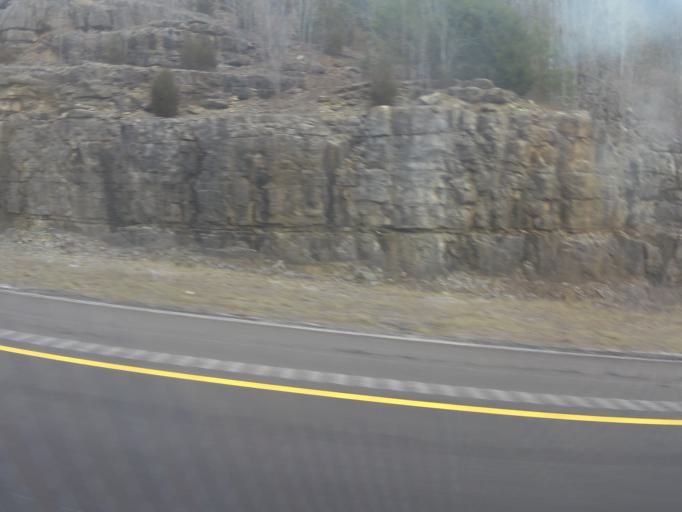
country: US
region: Tennessee
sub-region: Marion County
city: Monteagle
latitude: 35.1904
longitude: -85.8162
